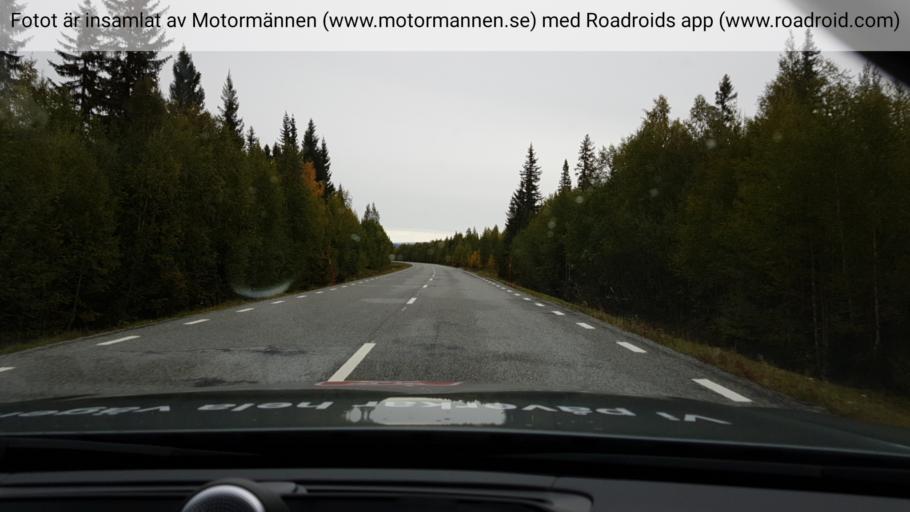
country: SE
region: Jaemtland
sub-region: Stroemsunds Kommun
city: Stroemsund
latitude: 64.1309
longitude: 15.6597
